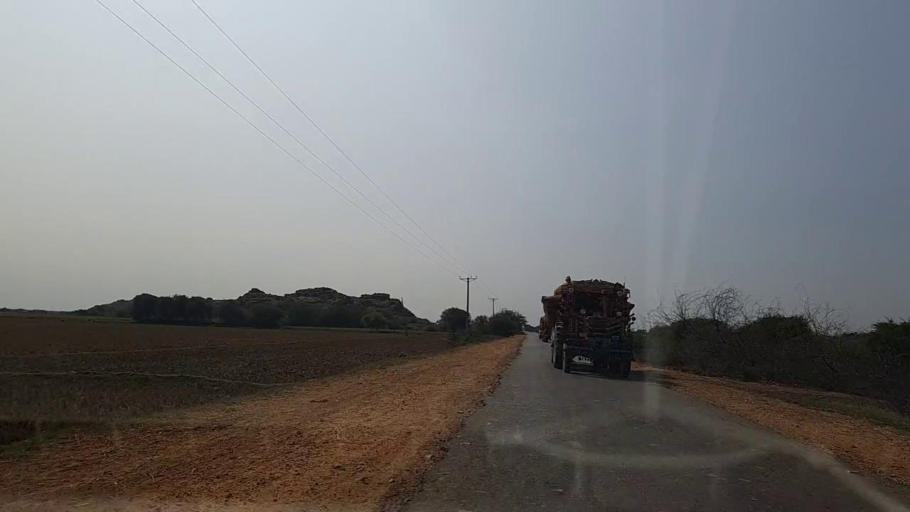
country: PK
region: Sindh
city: Chuhar Jamali
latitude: 24.3648
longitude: 67.9629
